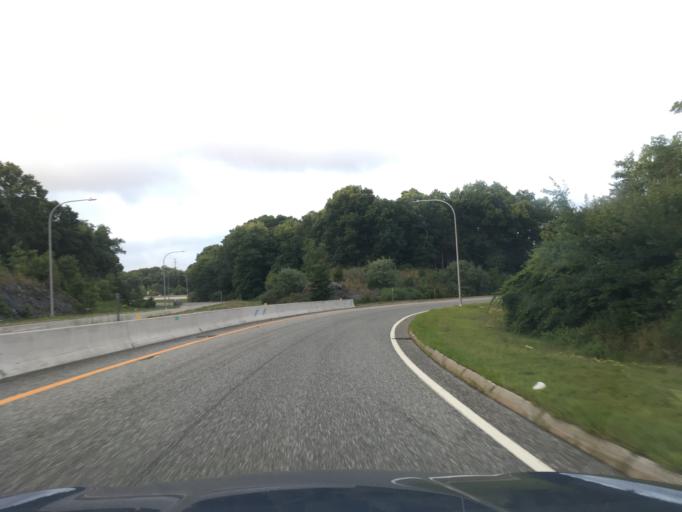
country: US
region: Rhode Island
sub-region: Kent County
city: East Greenwich
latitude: 41.6312
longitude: -71.4897
